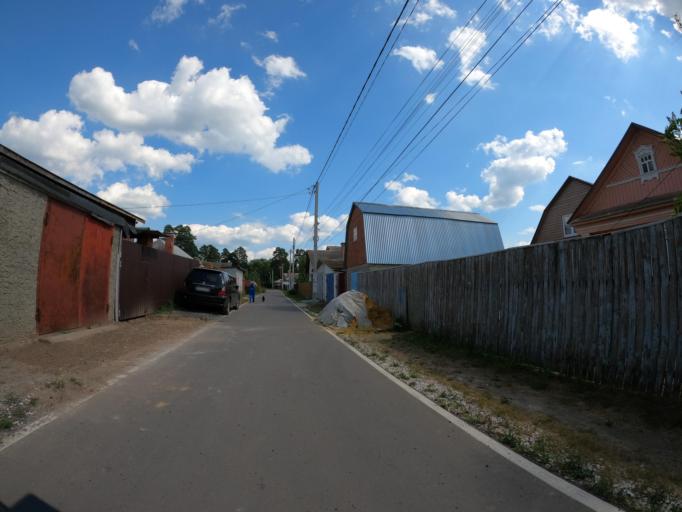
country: RU
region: Moskovskaya
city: Peski
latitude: 55.2654
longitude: 38.7561
